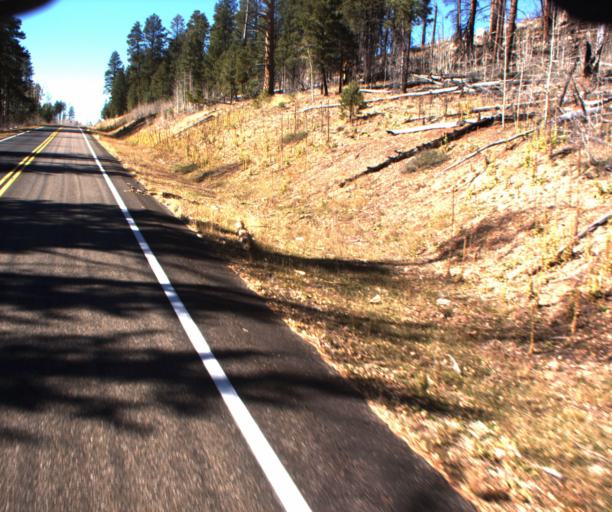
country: US
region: Arizona
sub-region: Coconino County
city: Grand Canyon
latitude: 36.5433
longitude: -112.1711
